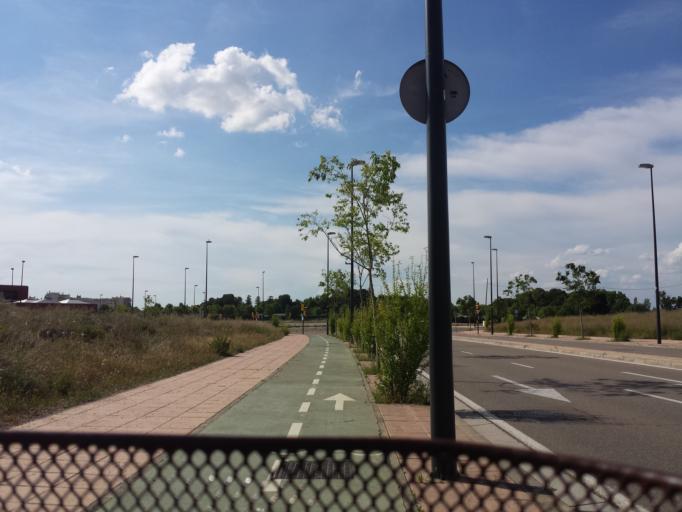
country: ES
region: Aragon
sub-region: Provincia de Zaragoza
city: Montecanal
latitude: 41.6349
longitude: -0.9382
